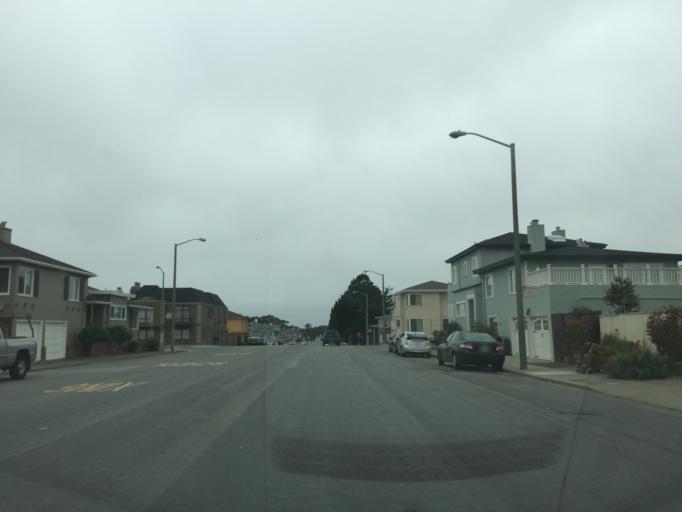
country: US
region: California
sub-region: San Mateo County
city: Daly City
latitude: 37.7322
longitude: -122.4873
